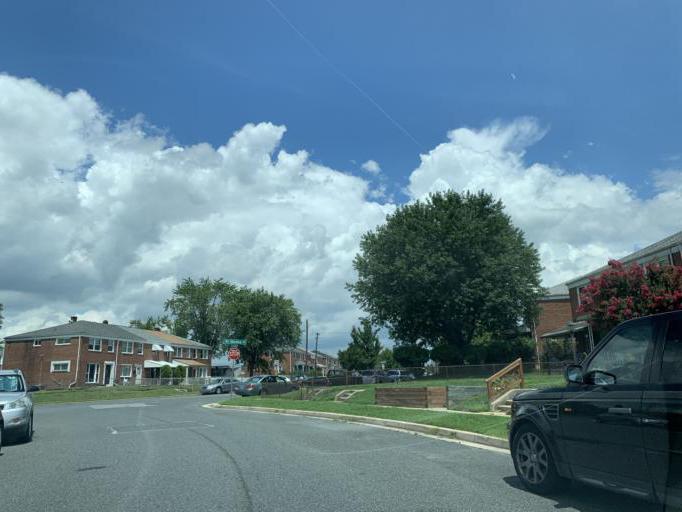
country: US
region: Maryland
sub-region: Baltimore County
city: Edgemere
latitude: 39.2659
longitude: -76.4729
